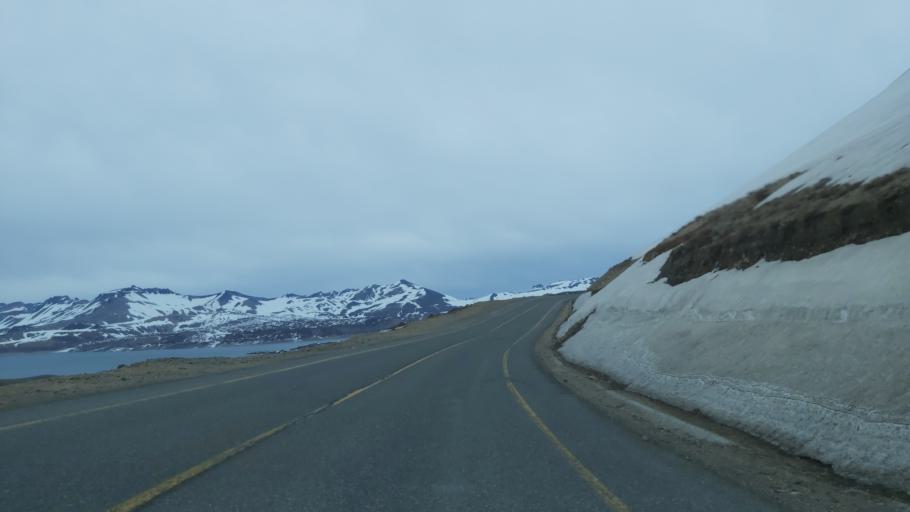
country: CL
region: Maule
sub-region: Provincia de Linares
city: Colbun
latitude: -36.0217
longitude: -70.5007
